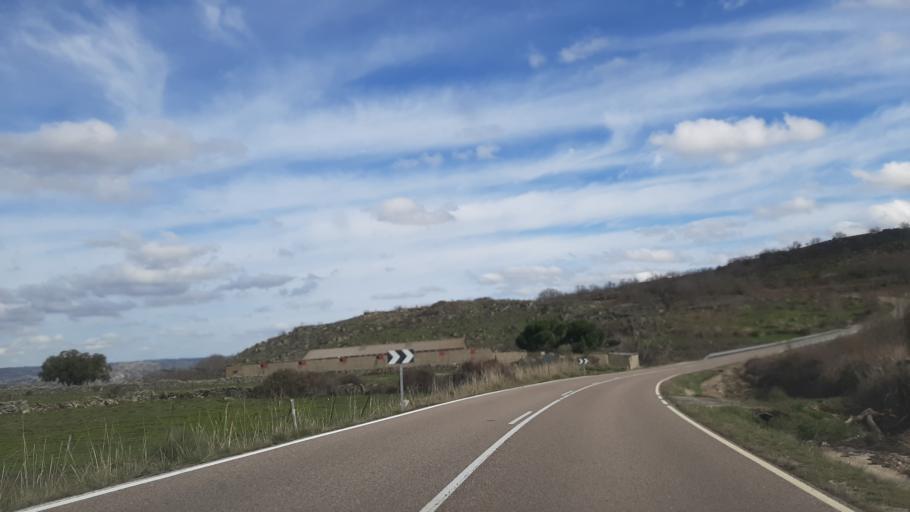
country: ES
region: Castille and Leon
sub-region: Provincia de Salamanca
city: Villarino de los Aires
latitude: 41.2636
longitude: -6.4367
